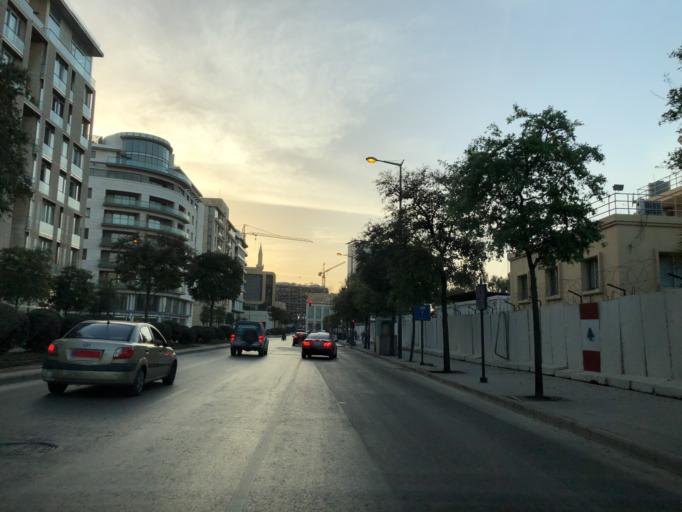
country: LB
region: Beyrouth
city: Beirut
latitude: 33.8999
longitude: 35.5077
